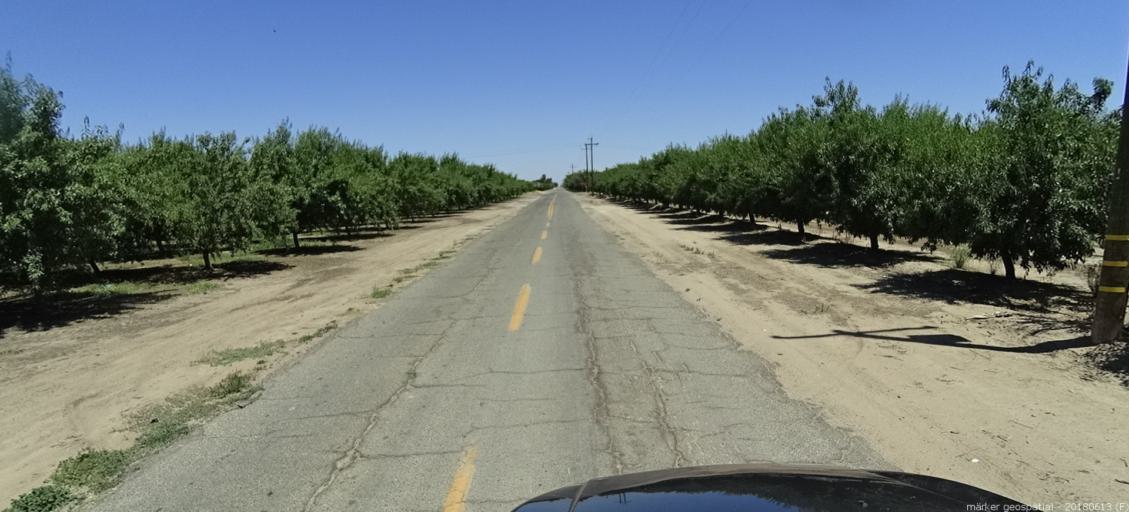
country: US
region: California
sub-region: Madera County
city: Fairmead
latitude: 36.9964
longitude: -120.2039
